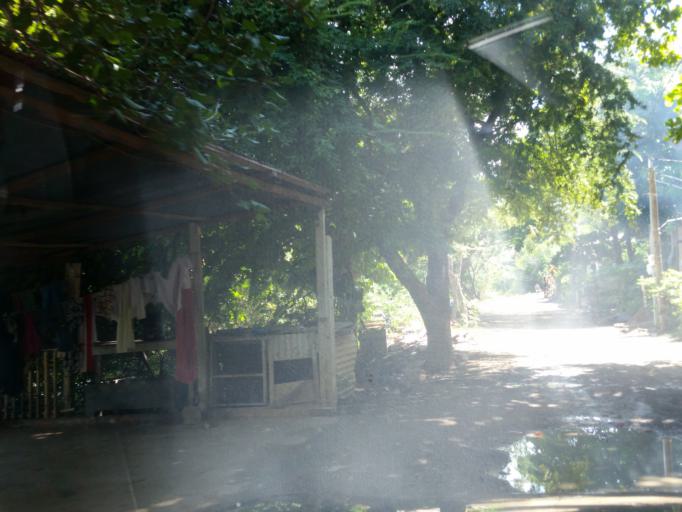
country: NI
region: Rivas
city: San Juan del Sur
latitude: 11.2577
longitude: -85.8711
